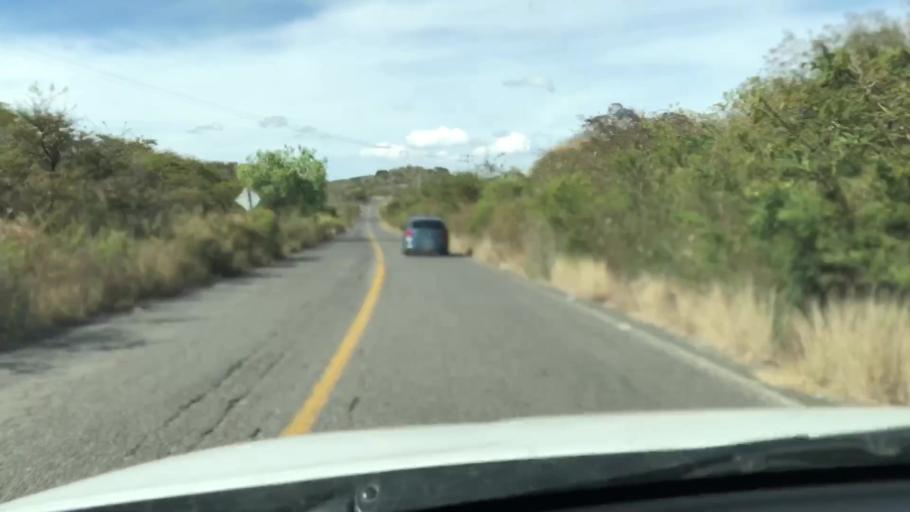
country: MX
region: Jalisco
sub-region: Zacoalco de Torres
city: Barranca de Otates (Barranca de Otatan)
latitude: 20.2083
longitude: -103.6929
